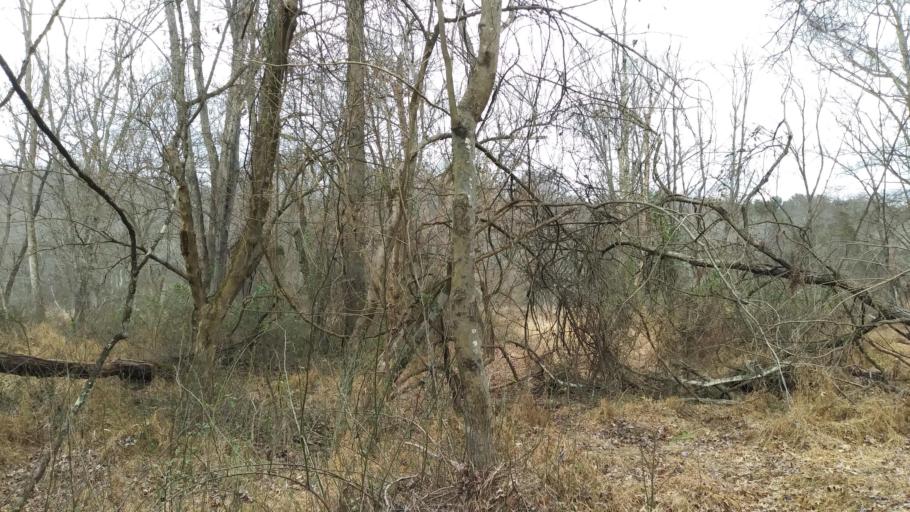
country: US
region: Pennsylvania
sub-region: York County
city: Susquehanna Trails
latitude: 39.6842
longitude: -76.2769
